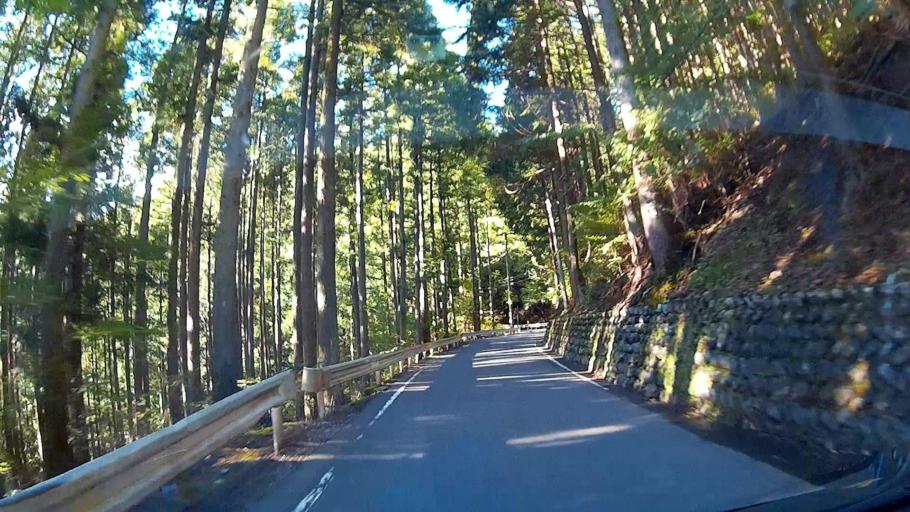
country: JP
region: Shizuoka
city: Shizuoka-shi
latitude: 35.1955
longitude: 138.2438
